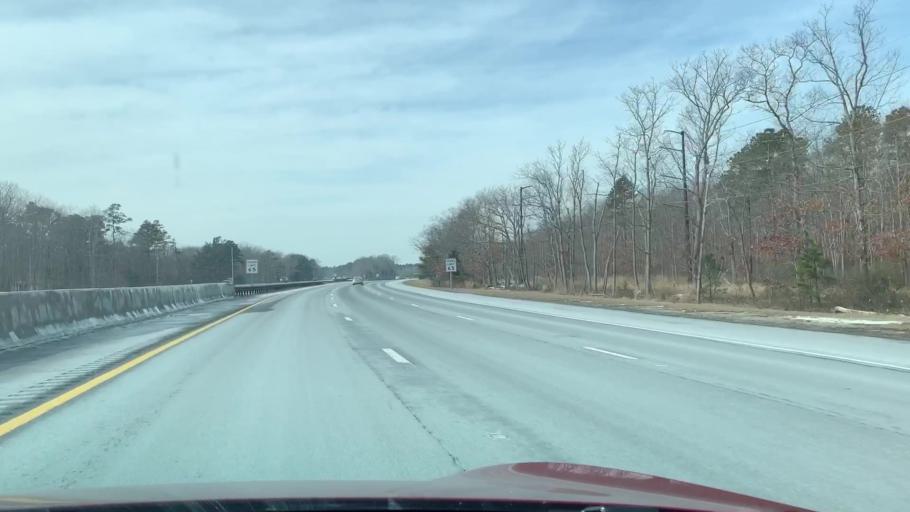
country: US
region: New Jersey
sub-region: Atlantic County
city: Port Republic
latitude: 39.5420
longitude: -74.4744
